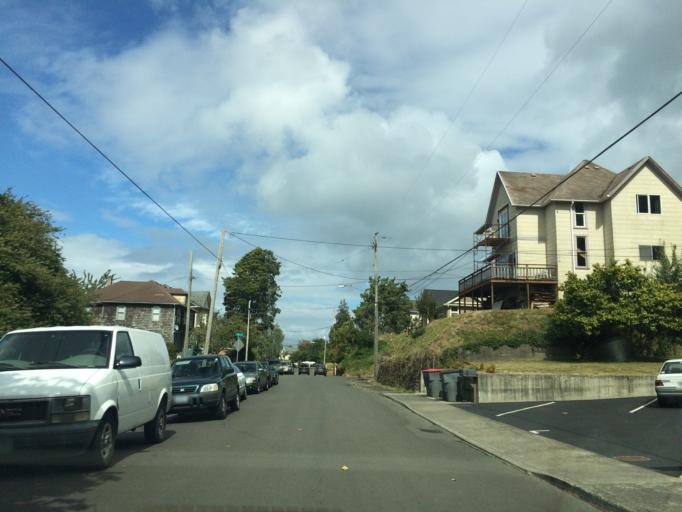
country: US
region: Oregon
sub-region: Clatsop County
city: Astoria
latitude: 46.1893
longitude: -123.8105
